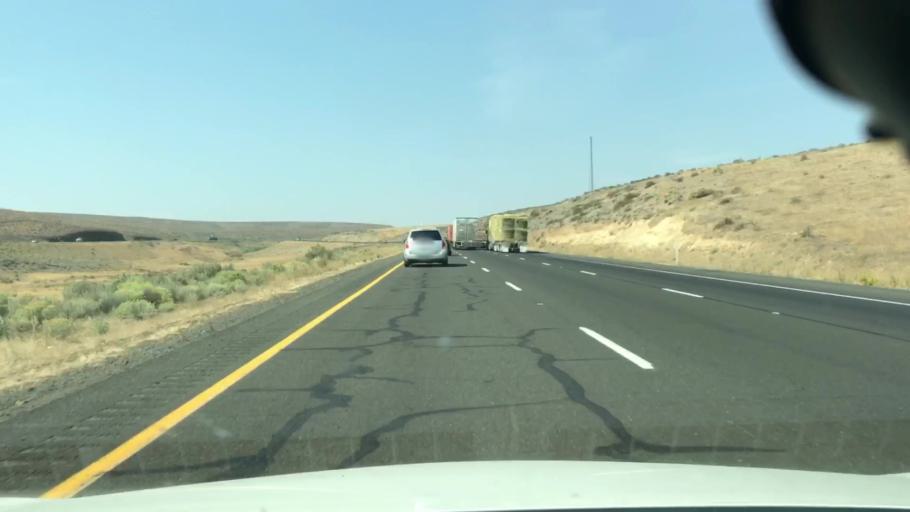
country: US
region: Washington
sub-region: Grant County
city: Mattawa
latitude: 46.9412
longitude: -120.0687
